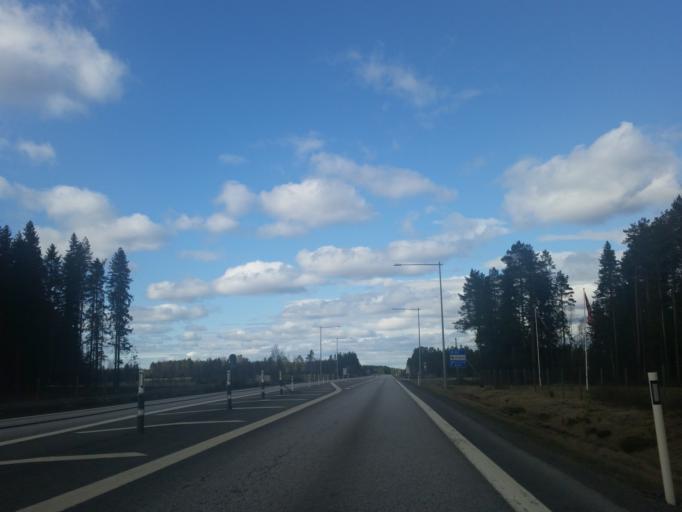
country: SE
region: Vaesterbotten
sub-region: Robertsfors Kommun
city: Robertsfors
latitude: 64.0889
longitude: 20.8689
